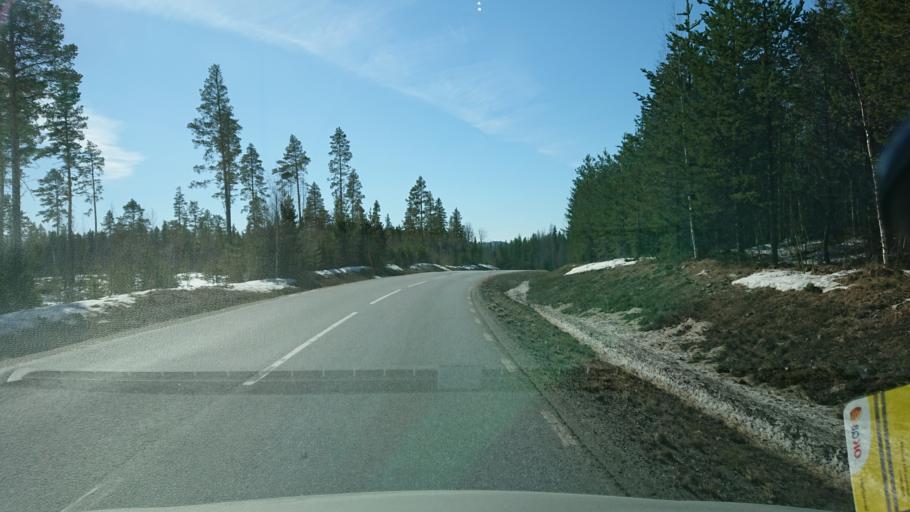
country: SE
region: Vaesterbotten
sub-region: Dorotea Kommun
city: Dorotea
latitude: 64.0183
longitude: 16.2892
